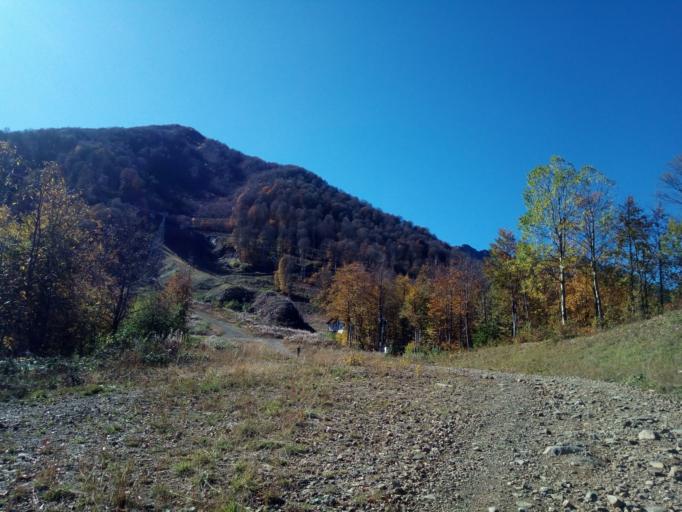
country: RU
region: Krasnodarskiy
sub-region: Sochi City
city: Krasnaya Polyana
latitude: 43.6451
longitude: 40.3124
